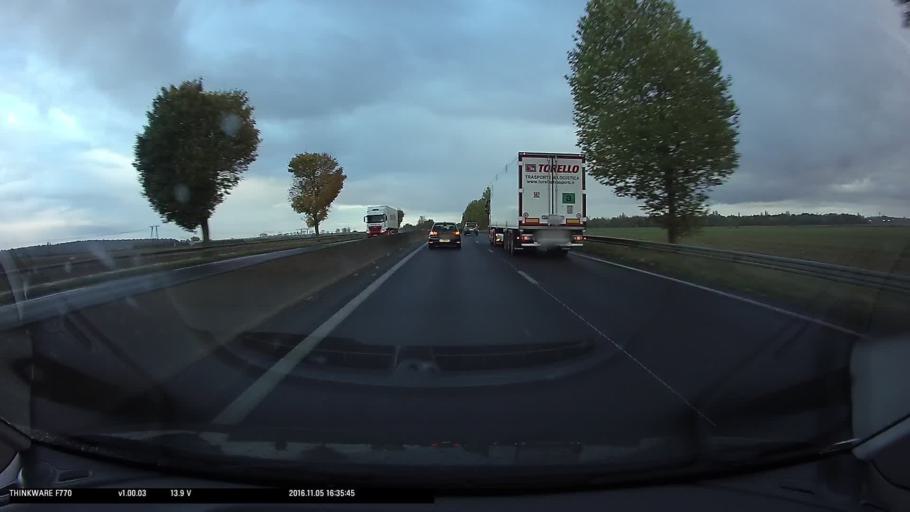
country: FR
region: Ile-de-France
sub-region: Departement du Val-d'Oise
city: Ableiges
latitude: 49.0624
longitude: 1.9881
